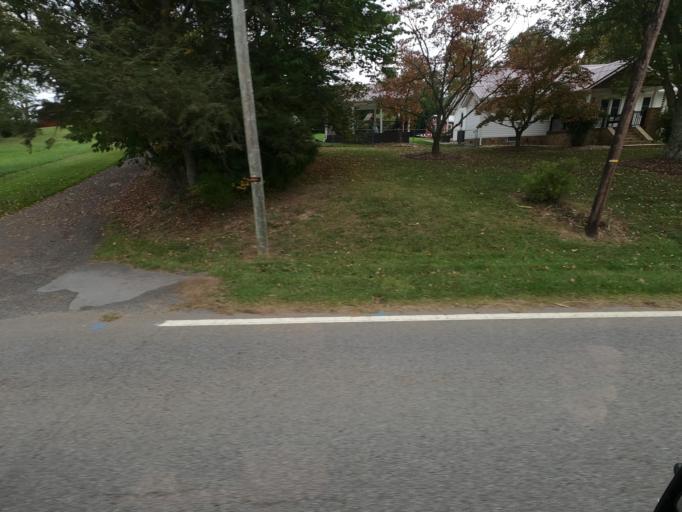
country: US
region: Tennessee
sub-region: Washington County
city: Jonesborough
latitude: 36.2360
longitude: -82.5573
